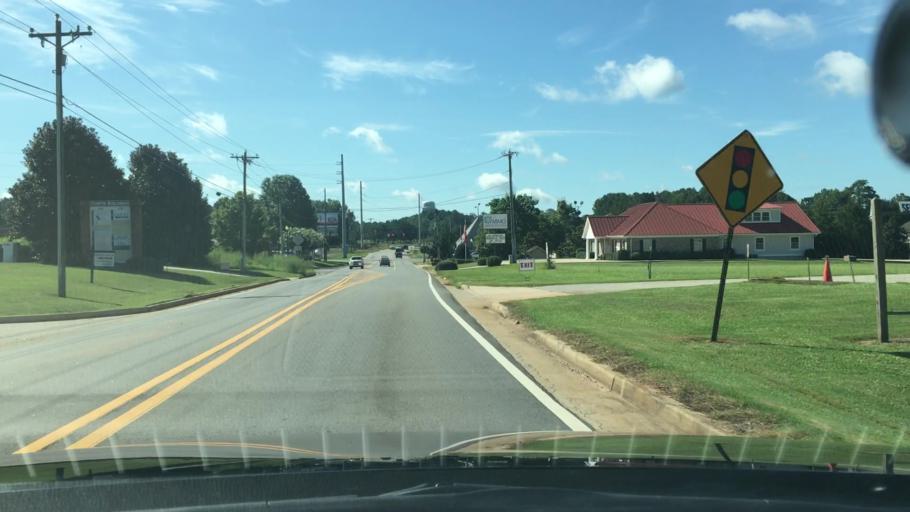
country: US
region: Georgia
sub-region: Putnam County
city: Jefferson
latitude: 33.4231
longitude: -83.2700
